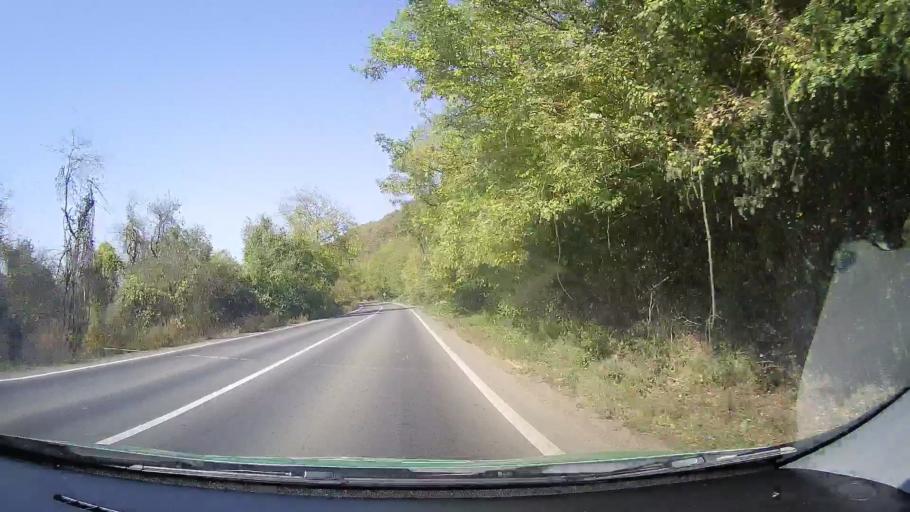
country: RO
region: Arad
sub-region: Comuna Savarsin
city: Savarsin
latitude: 45.9990
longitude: 22.2886
